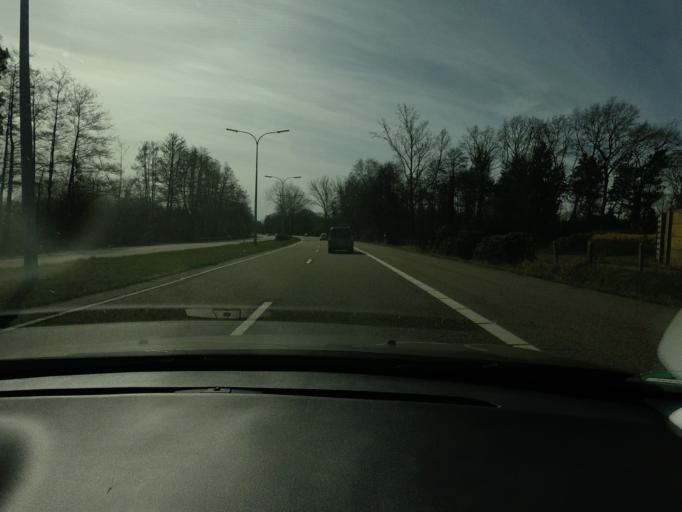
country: BE
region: Flanders
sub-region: Provincie Limburg
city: Zonhoven
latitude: 50.9909
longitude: 5.3592
